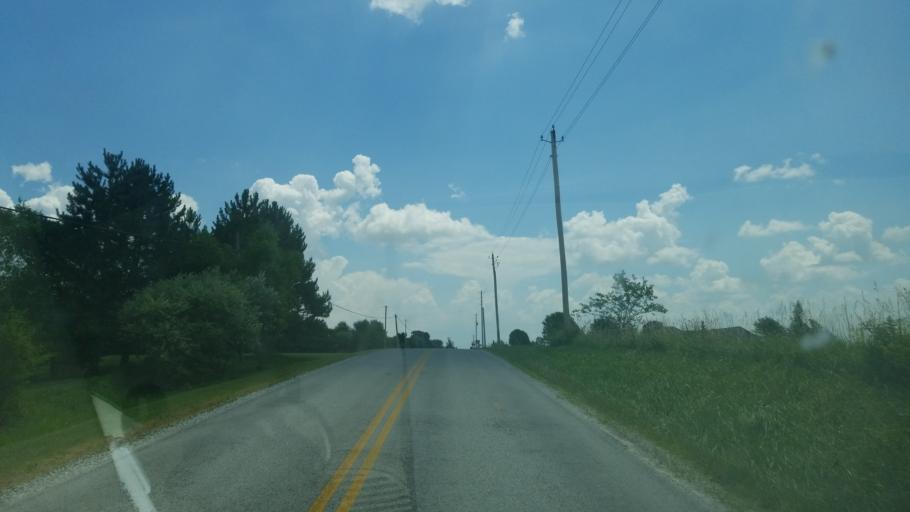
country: US
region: Ohio
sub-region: Hardin County
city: Kenton
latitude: 40.6625
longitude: -83.6604
